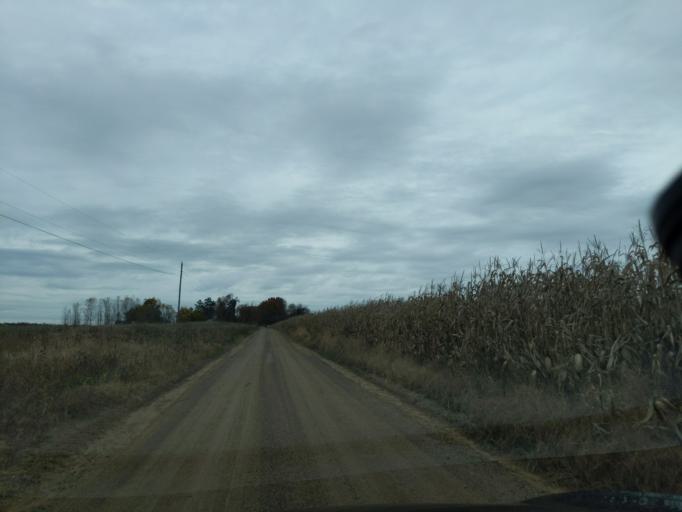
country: US
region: Michigan
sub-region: Eaton County
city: Eaton Rapids
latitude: 42.4257
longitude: -84.6005
